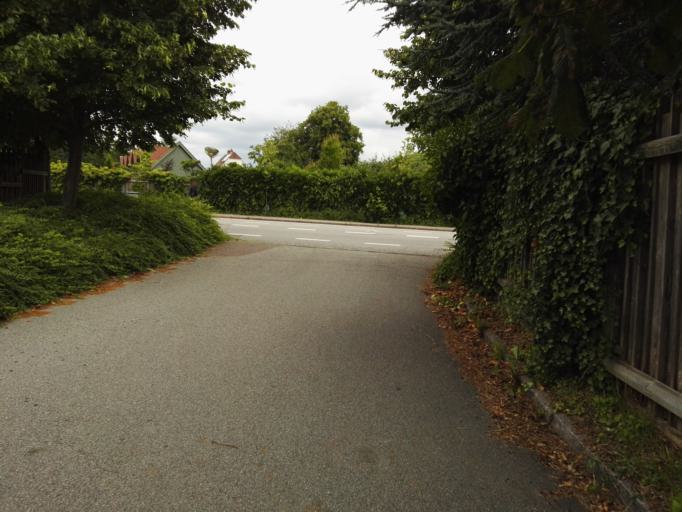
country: DK
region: Capital Region
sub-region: Egedal Kommune
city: Olstykke
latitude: 55.7951
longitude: 12.1564
